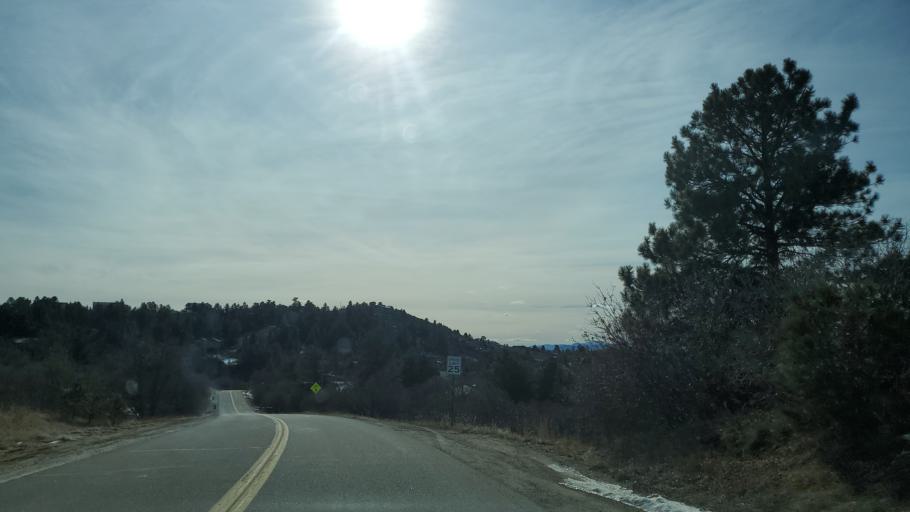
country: US
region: Colorado
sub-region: Douglas County
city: Castle Pines
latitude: 39.4476
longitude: -104.8724
